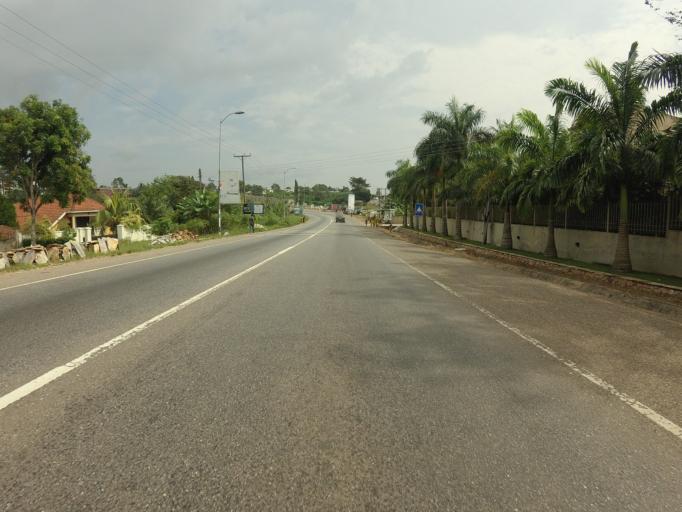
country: GH
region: Eastern
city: Aburi
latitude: 5.8087
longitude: -0.1842
